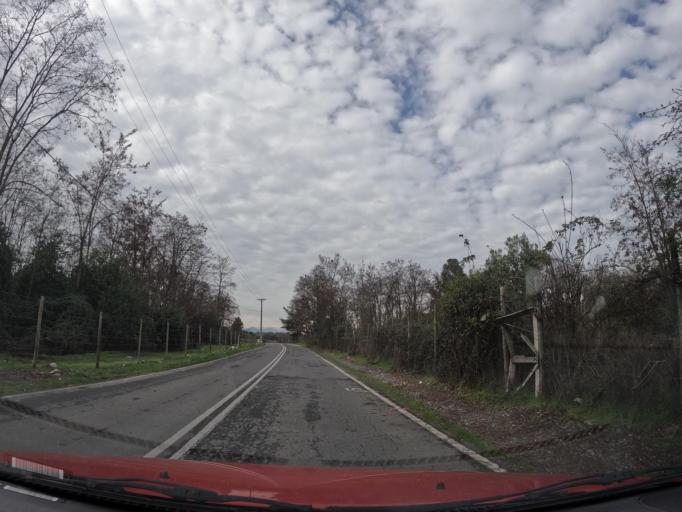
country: CL
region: Maule
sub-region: Provincia de Linares
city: Linares
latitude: -35.8660
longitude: -71.6246
